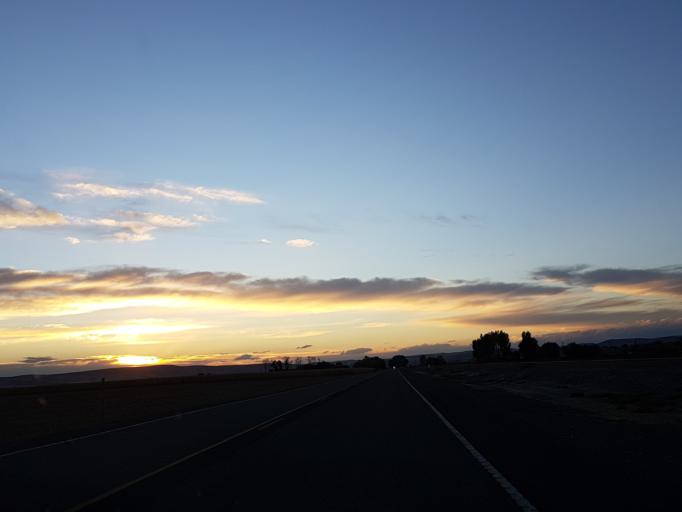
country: US
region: Oregon
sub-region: Malheur County
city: Vale
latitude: 43.9363
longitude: -117.3187
